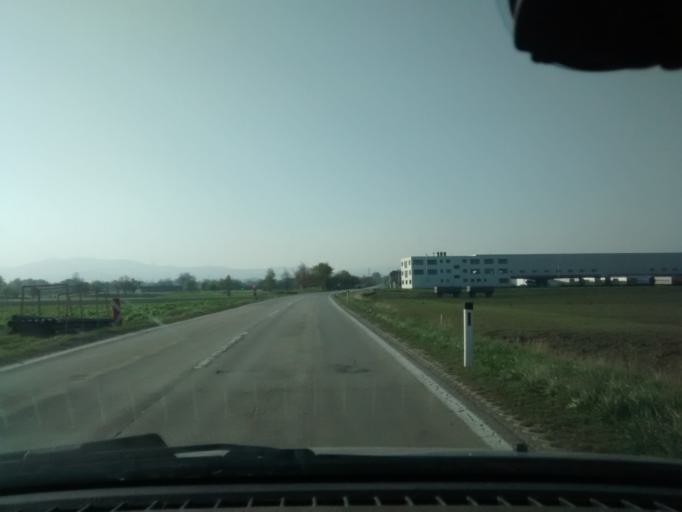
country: AT
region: Lower Austria
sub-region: Politischer Bezirk Modling
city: Achau
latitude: 48.0811
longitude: 16.3739
